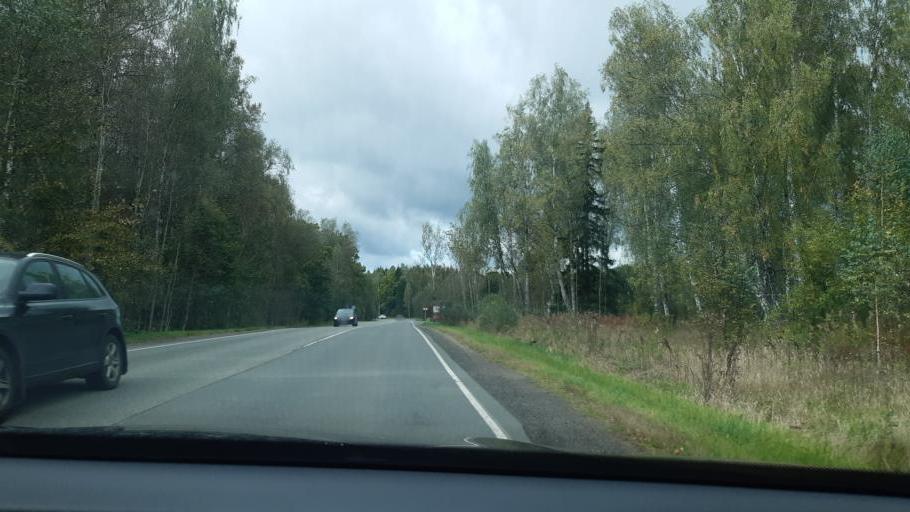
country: RU
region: Moskovskaya
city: Melikhovo
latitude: 55.1200
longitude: 37.6311
